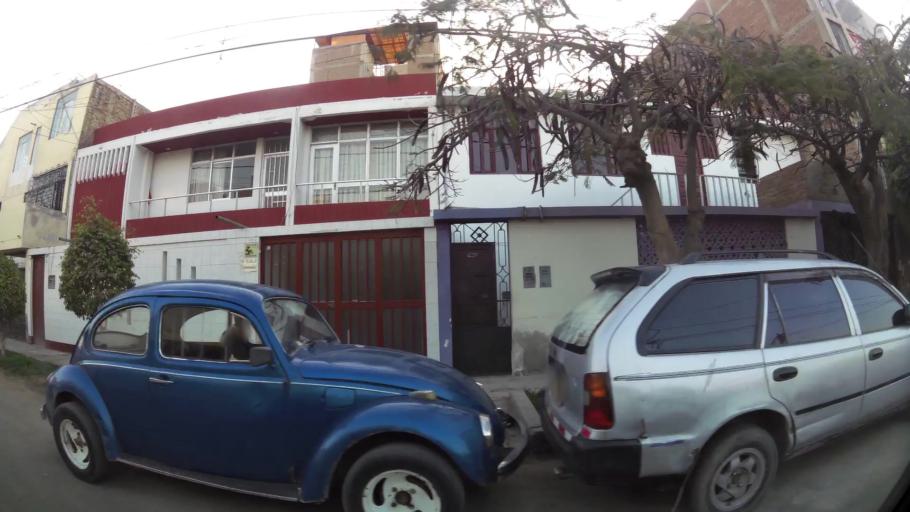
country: PE
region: Lambayeque
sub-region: Provincia de Chiclayo
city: Santa Rosa
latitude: -6.7677
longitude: -79.8341
